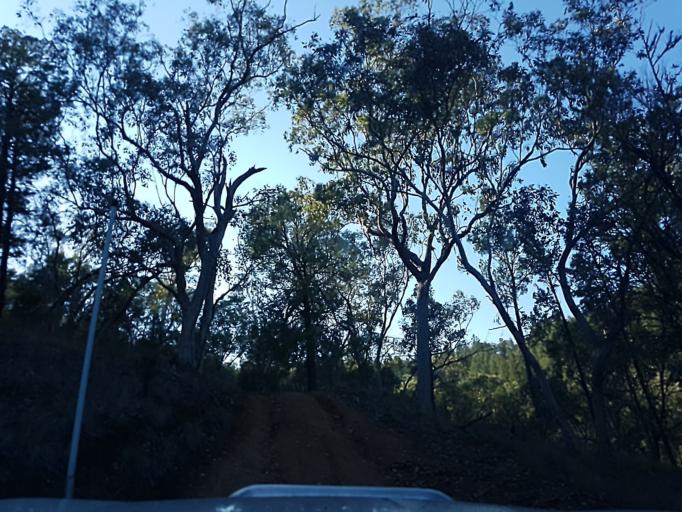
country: AU
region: New South Wales
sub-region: Snowy River
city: Jindabyne
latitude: -36.9539
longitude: 148.3810
